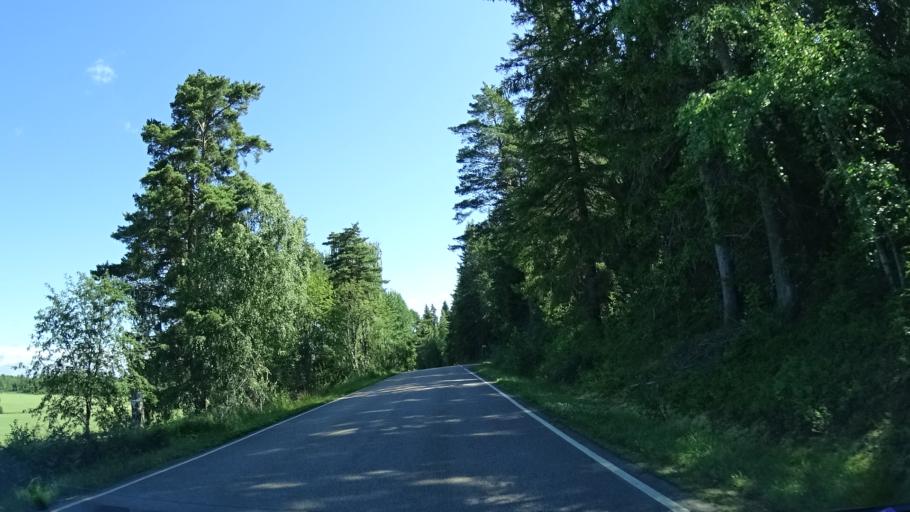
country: FI
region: Varsinais-Suomi
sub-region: Turku
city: Askainen
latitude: 60.5273
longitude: 21.8420
